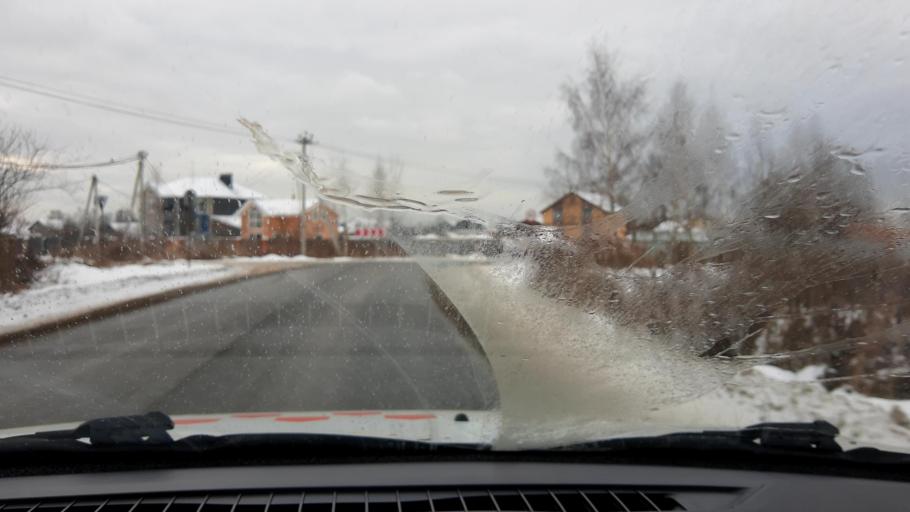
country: RU
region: Nizjnij Novgorod
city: Neklyudovo
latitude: 56.4251
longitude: 43.9632
